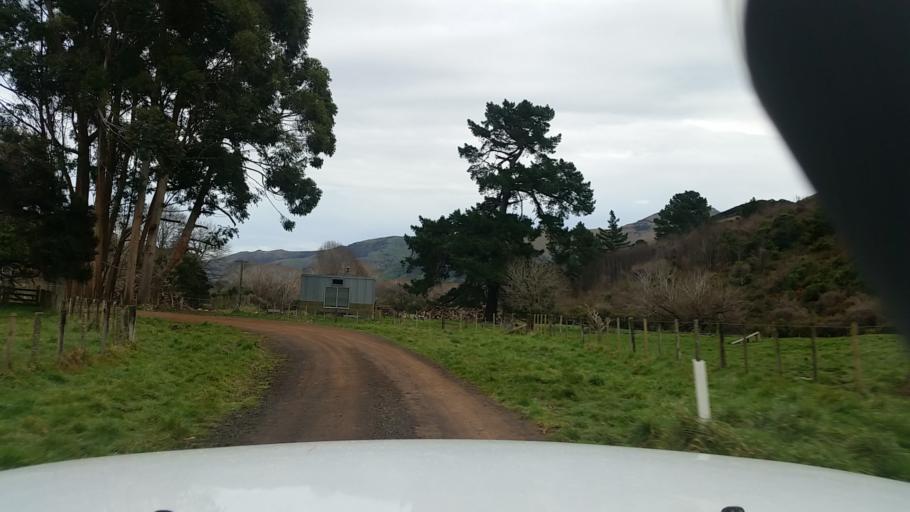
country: NZ
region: Canterbury
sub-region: Christchurch City
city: Christchurch
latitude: -43.7860
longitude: 172.8187
